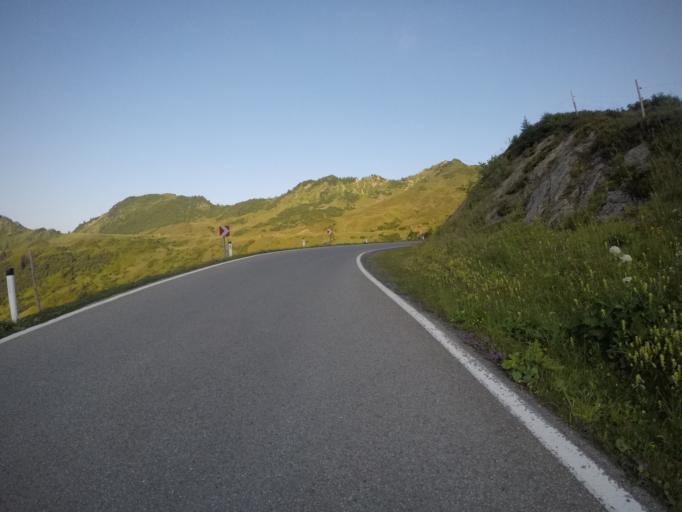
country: AT
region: Vorarlberg
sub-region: Politischer Bezirk Bregenz
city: Damuels
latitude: 47.2765
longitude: 9.8416
